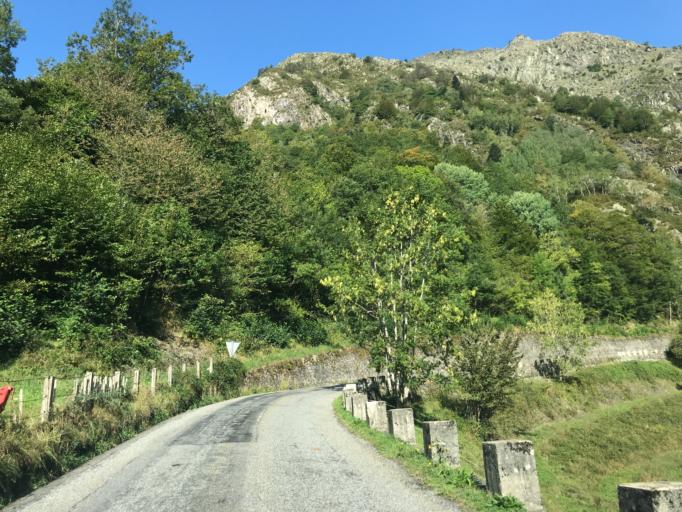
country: FR
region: Midi-Pyrenees
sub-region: Departement des Hautes-Pyrenees
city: Saint-Lary-Soulan
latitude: 42.7915
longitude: 0.2267
